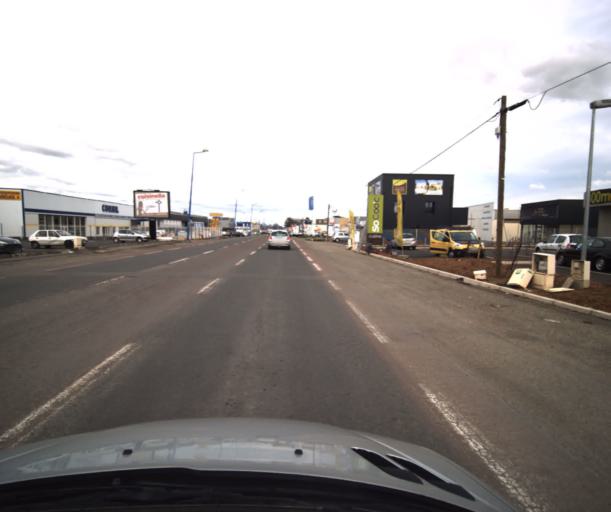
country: FR
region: Midi-Pyrenees
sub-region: Departement du Tarn-et-Garonne
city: Montauban
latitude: 44.0316
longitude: 1.3732
